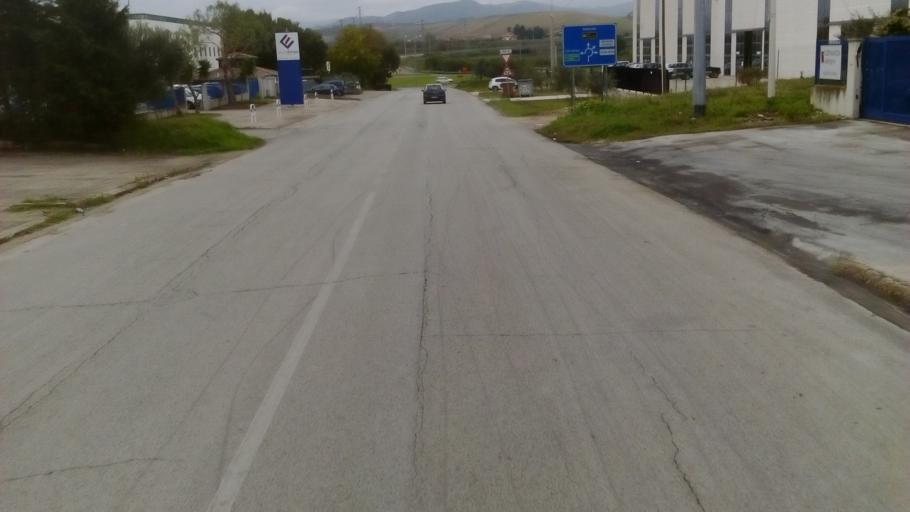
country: IT
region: Abruzzo
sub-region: Provincia di Chieti
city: San Salvo
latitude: 42.0349
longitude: 14.7431
